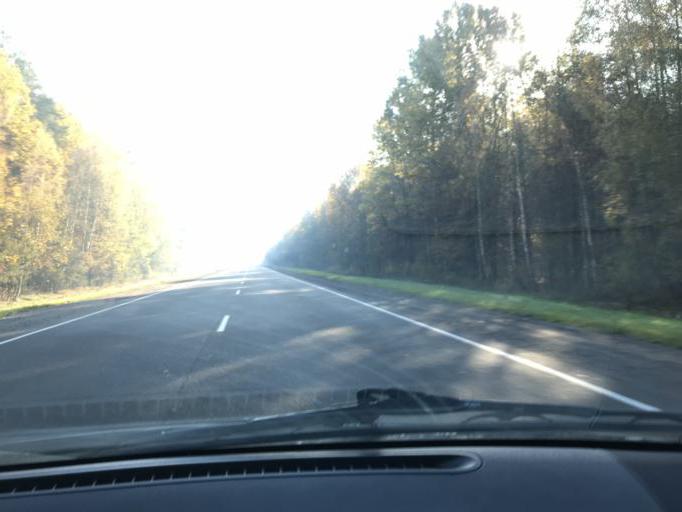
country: BY
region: Brest
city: Horad Luninyets
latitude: 52.3054
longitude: 26.6971
